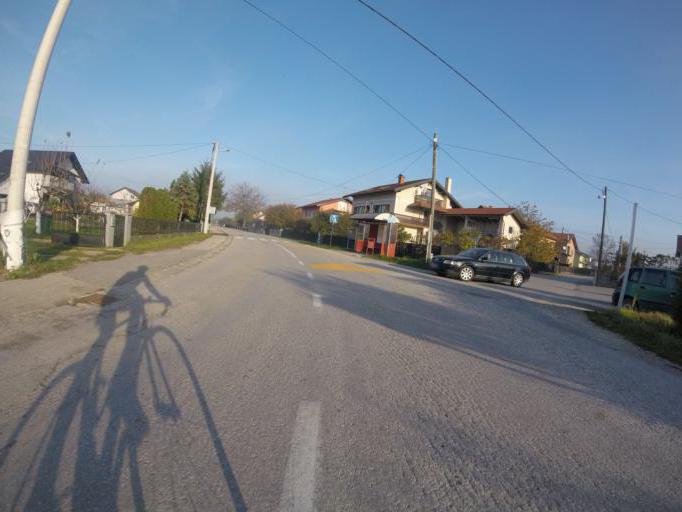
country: HR
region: Zagrebacka
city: Micevec
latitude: 45.7509
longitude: 16.0969
